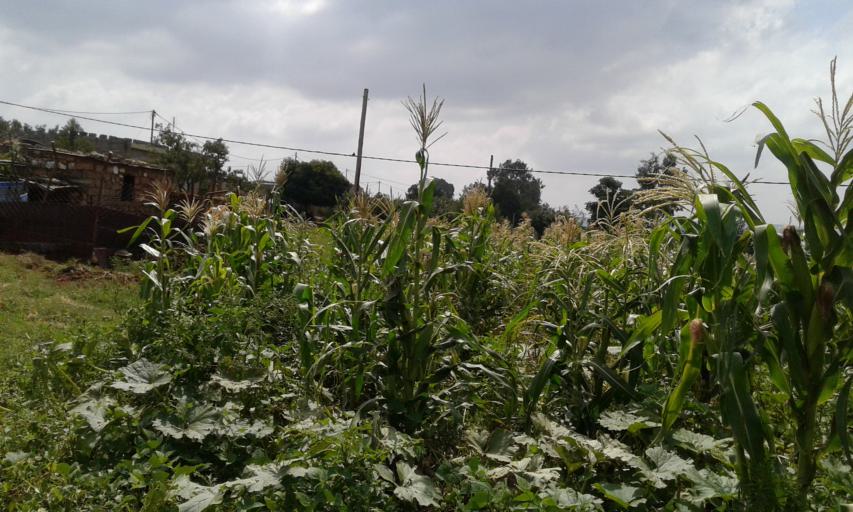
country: LS
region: Maseru
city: Maseru
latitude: -29.4287
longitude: 27.5746
